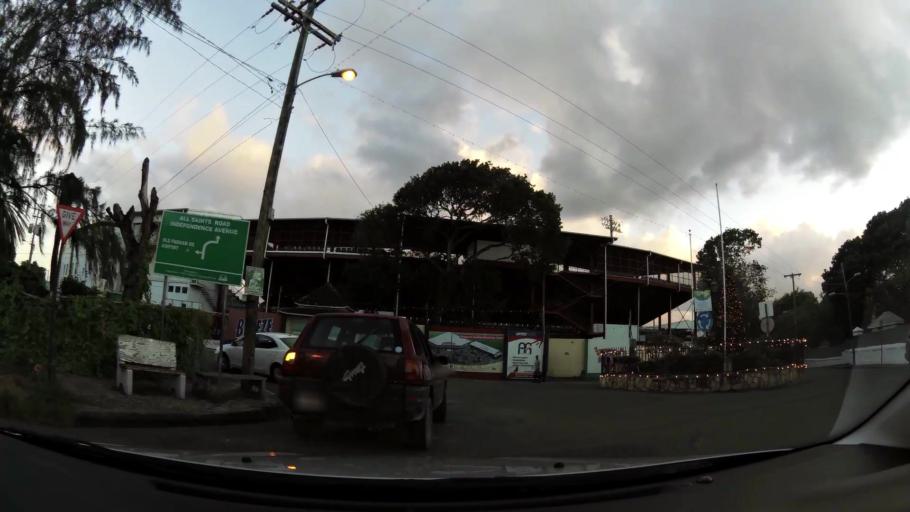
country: AG
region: Saint John
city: Saint John's
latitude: 17.1233
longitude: -61.8396
